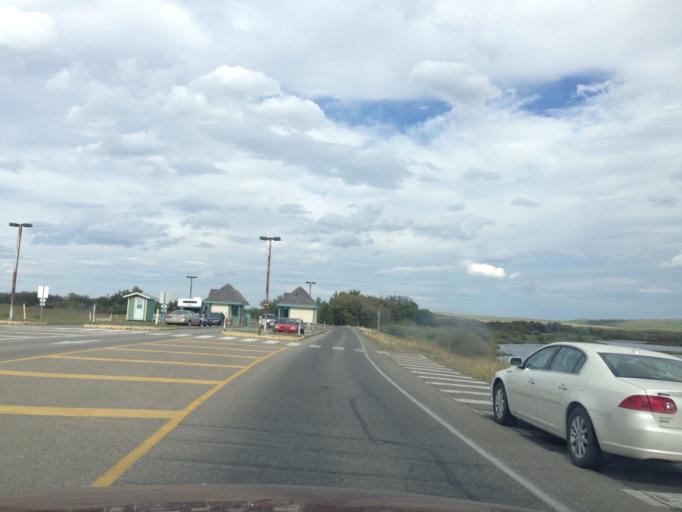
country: CA
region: Alberta
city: Pincher Creek
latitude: 49.1091
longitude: -113.8502
